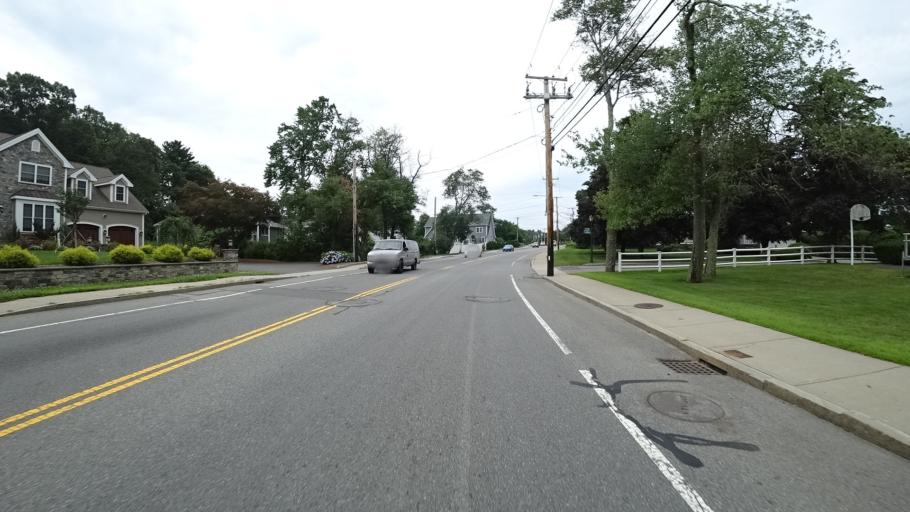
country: US
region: Massachusetts
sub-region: Norfolk County
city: Dedham
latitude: 42.2274
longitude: -71.1621
